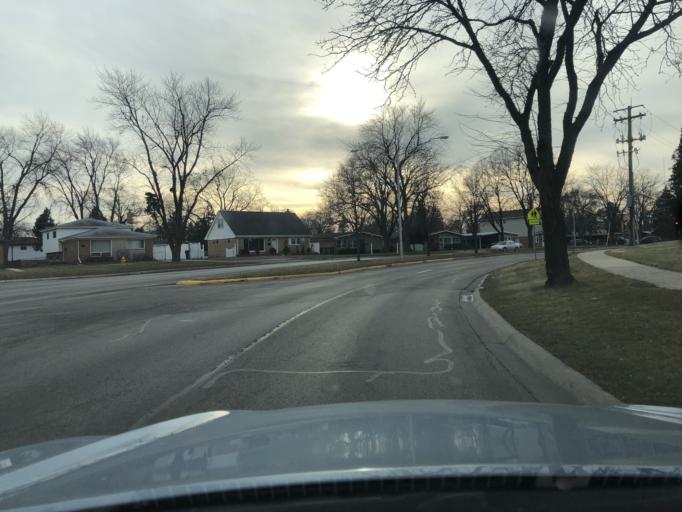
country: US
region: Illinois
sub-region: DuPage County
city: Addison
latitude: 41.9322
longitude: -87.9945
